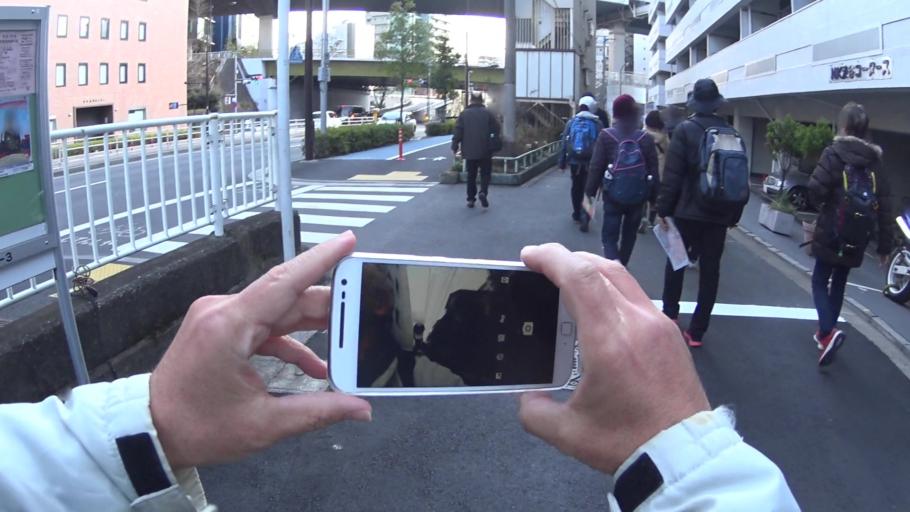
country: JP
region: Tokyo
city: Tokyo
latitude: 35.6540
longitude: 139.6890
